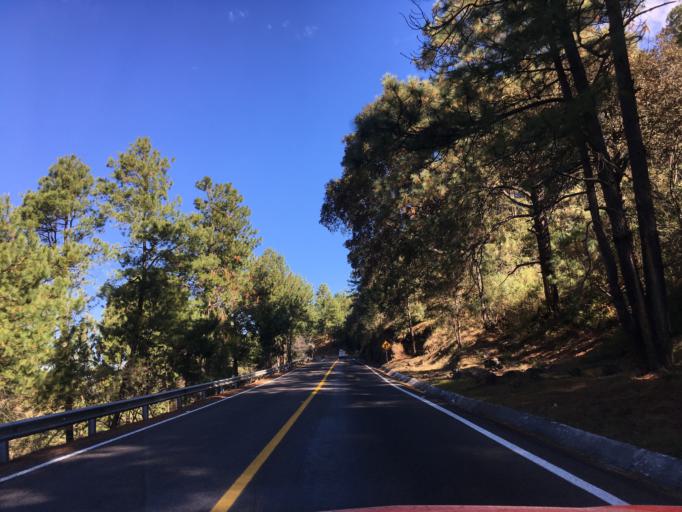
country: MX
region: Michoacan
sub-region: Hidalgo
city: Tierras Coloradas (San Pedro)
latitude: 19.6708
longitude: -100.7295
